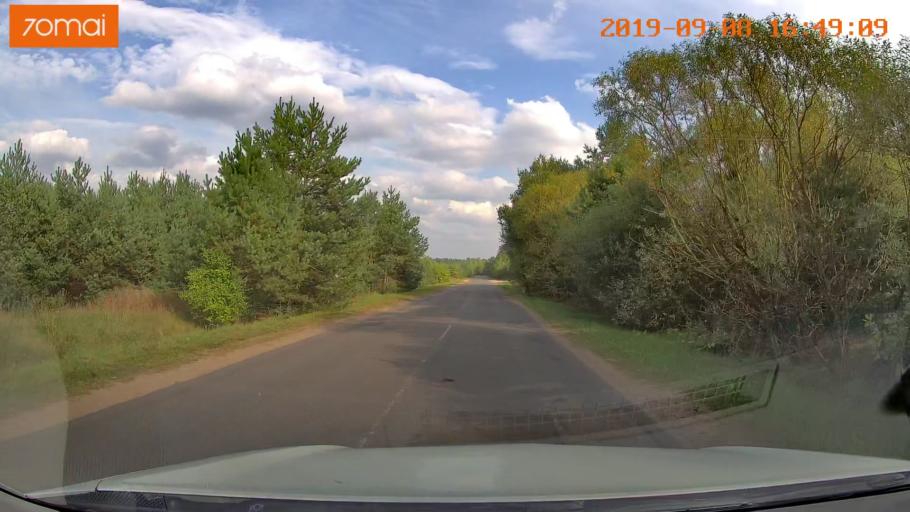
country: BY
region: Grodnenskaya
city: Hrodna
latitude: 53.8108
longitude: 23.8682
